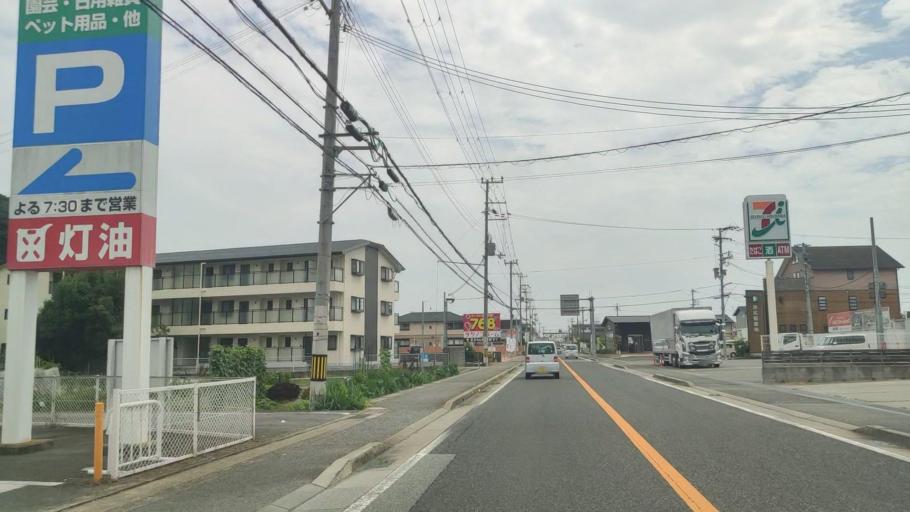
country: JP
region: Hyogo
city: Tatsunocho-tominaga
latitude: 34.8717
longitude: 134.5542
